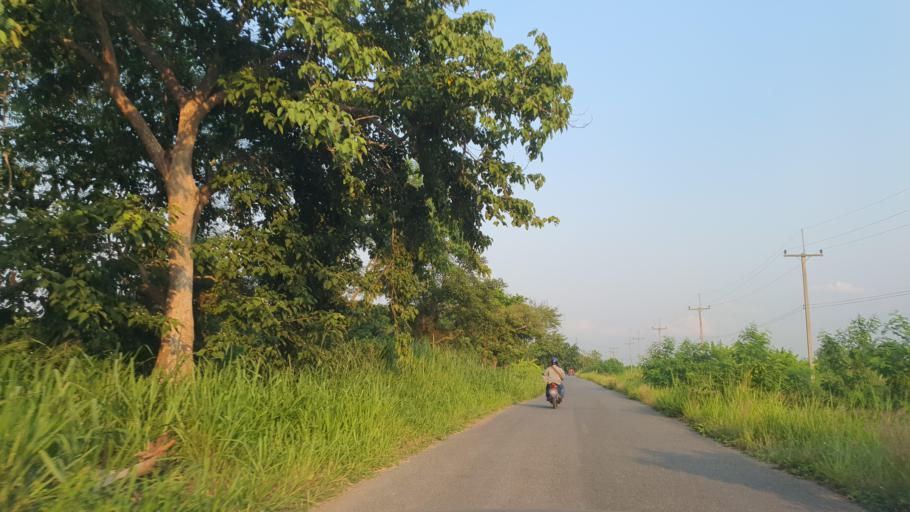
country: TH
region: Chiang Mai
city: Hang Dong
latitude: 18.6584
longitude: 98.9274
